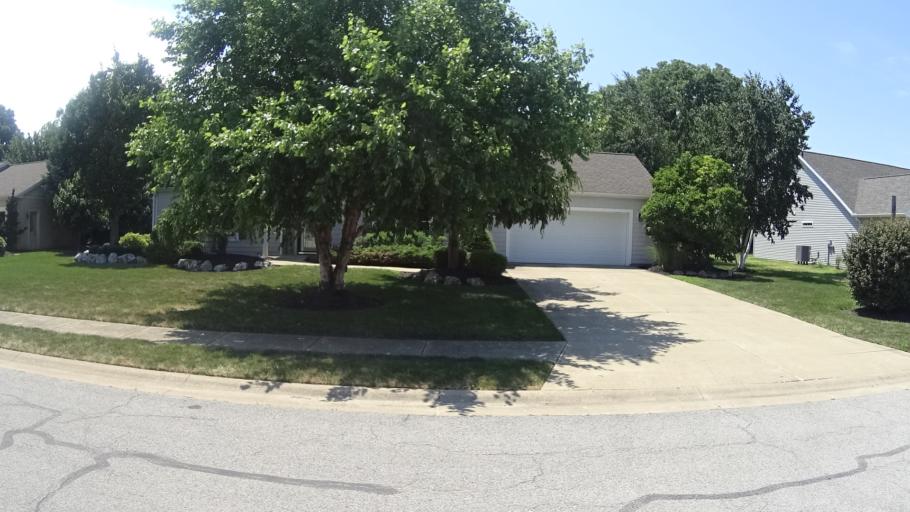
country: US
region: Ohio
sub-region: Erie County
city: Sandusky
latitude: 41.4223
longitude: -82.6467
